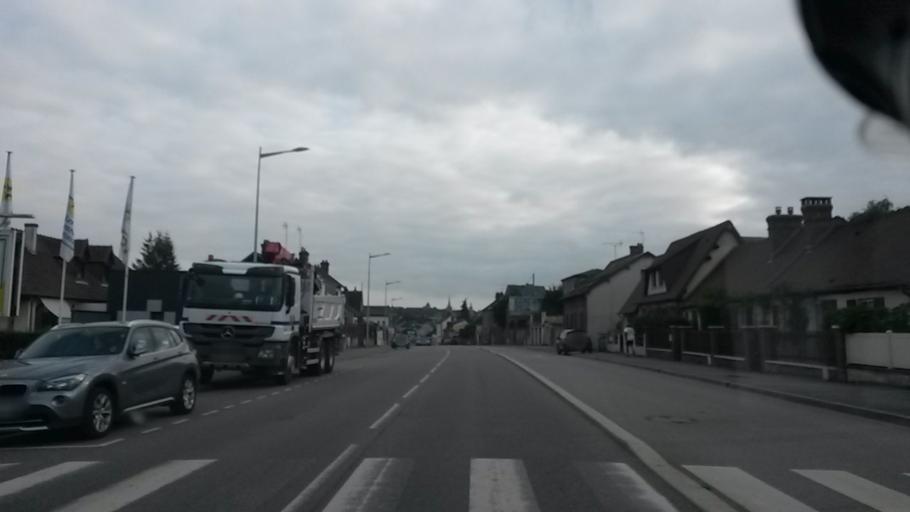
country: FR
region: Haute-Normandie
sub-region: Departement de l'Eure
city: Evreux
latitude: 49.0371
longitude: 1.1569
